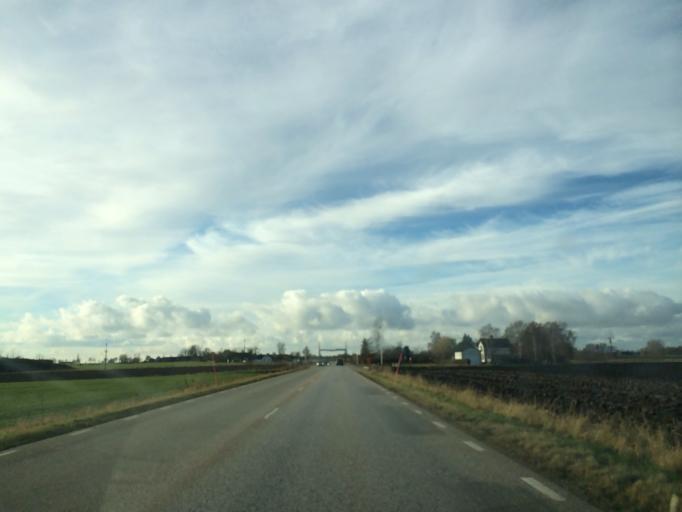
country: SE
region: Skane
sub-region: Lomma Kommun
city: Lomma
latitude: 55.7200
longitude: 13.0789
